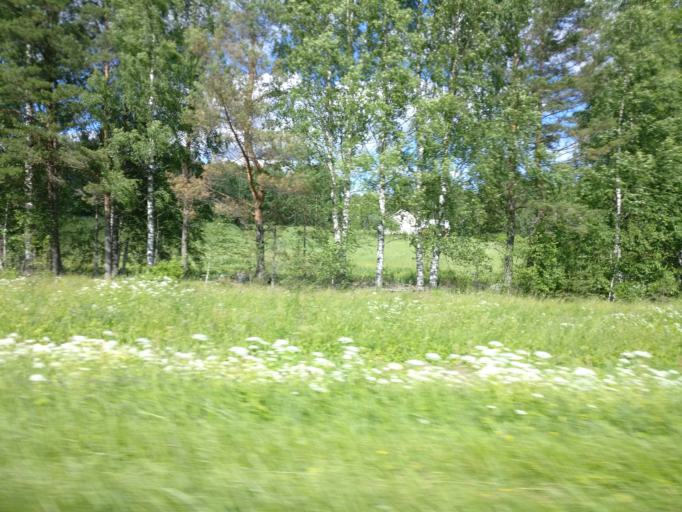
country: FI
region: Southern Savonia
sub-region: Savonlinna
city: Kerimaeki
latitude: 61.8671
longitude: 29.1341
